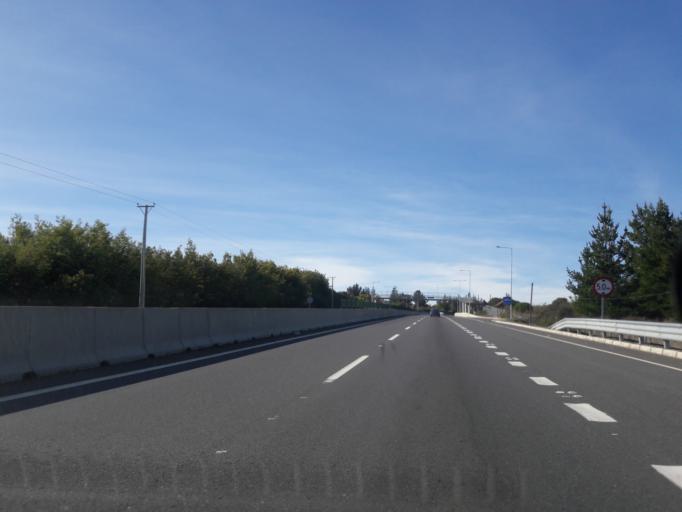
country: CL
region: Biobio
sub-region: Provincia de Biobio
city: Yumbel
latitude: -36.9742
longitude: -72.6582
